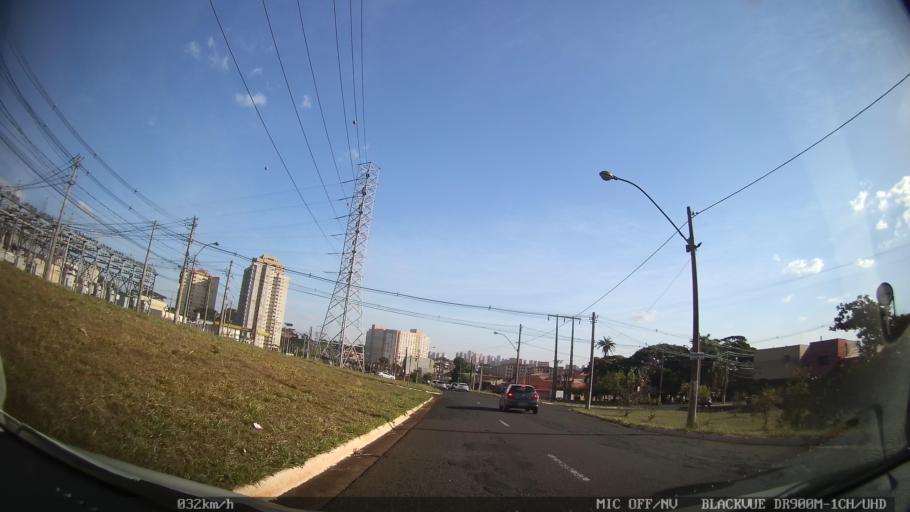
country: BR
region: Sao Paulo
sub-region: Ribeirao Preto
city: Ribeirao Preto
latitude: -21.1944
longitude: -47.7772
